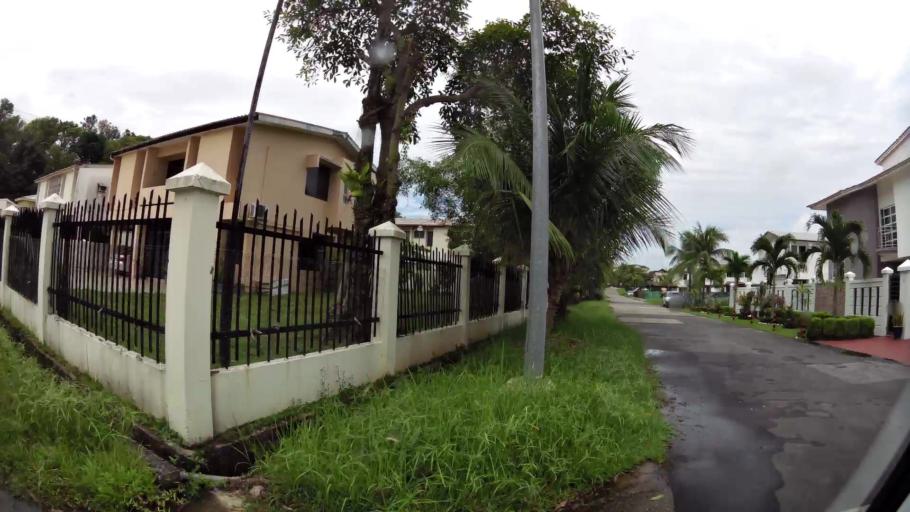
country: BN
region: Brunei and Muara
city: Bandar Seri Begawan
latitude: 4.8962
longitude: 114.9224
